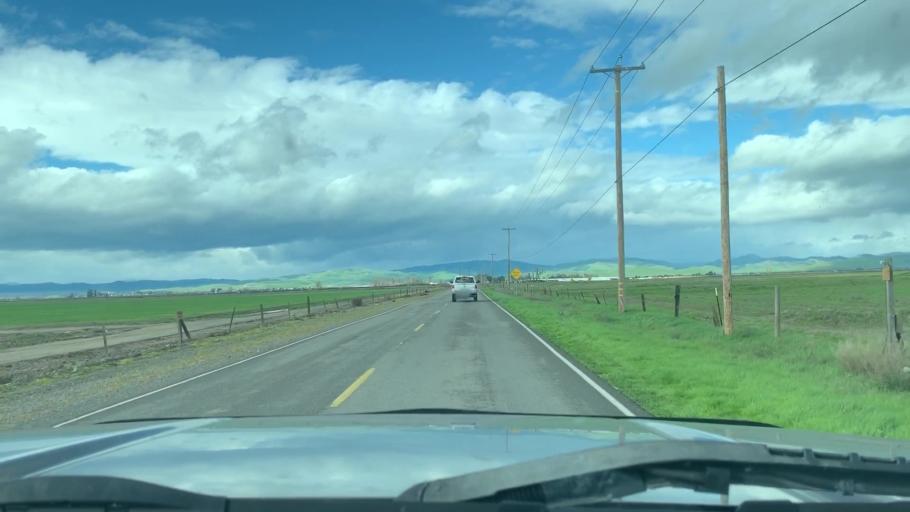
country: US
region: California
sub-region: Merced County
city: Los Banos
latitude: 37.1230
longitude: -120.9564
